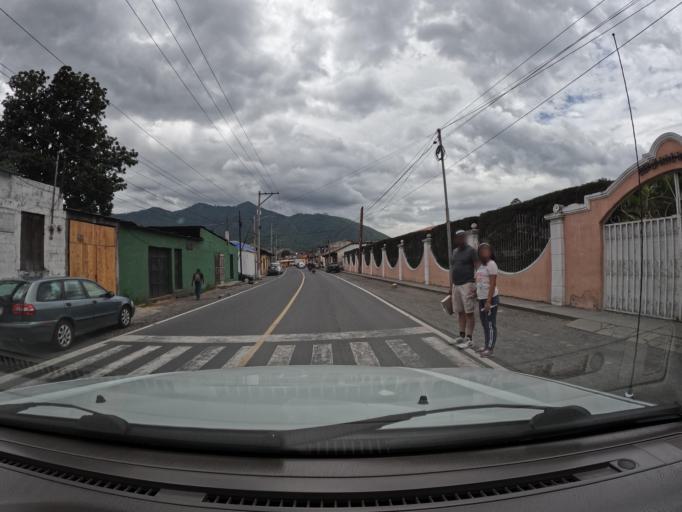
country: GT
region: Sacatepequez
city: Antigua Guatemala
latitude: 14.5669
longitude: -90.7354
